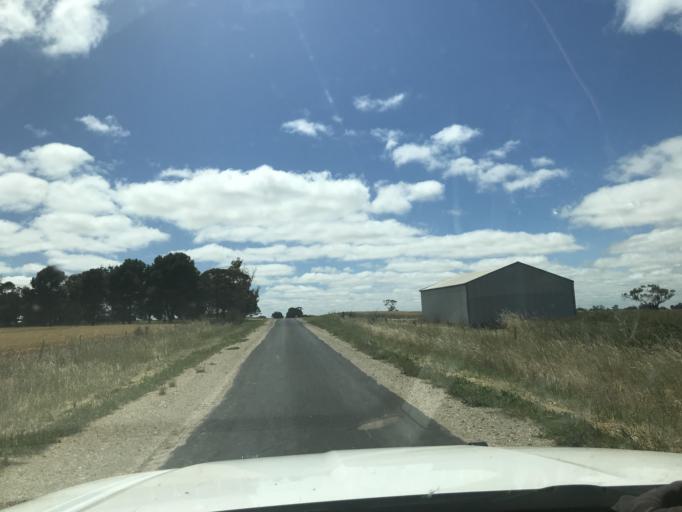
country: AU
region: South Australia
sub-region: Tatiara
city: Bordertown
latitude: -36.2804
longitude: 141.1346
